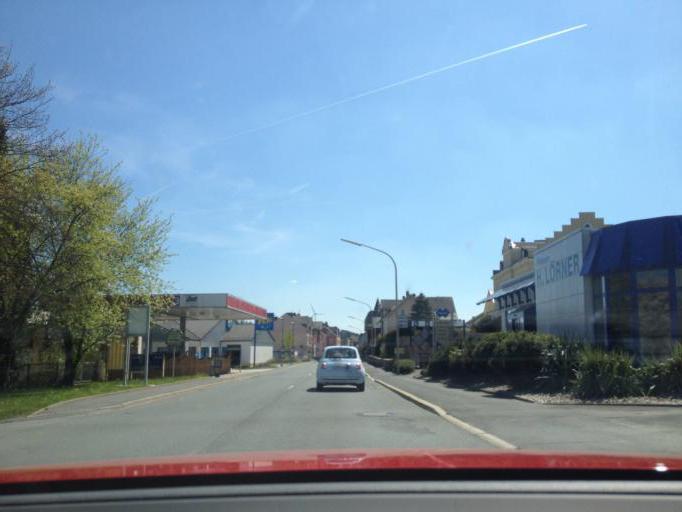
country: DE
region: Bavaria
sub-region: Upper Franconia
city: Oberkotzau
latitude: 50.2682
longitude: 11.9270
